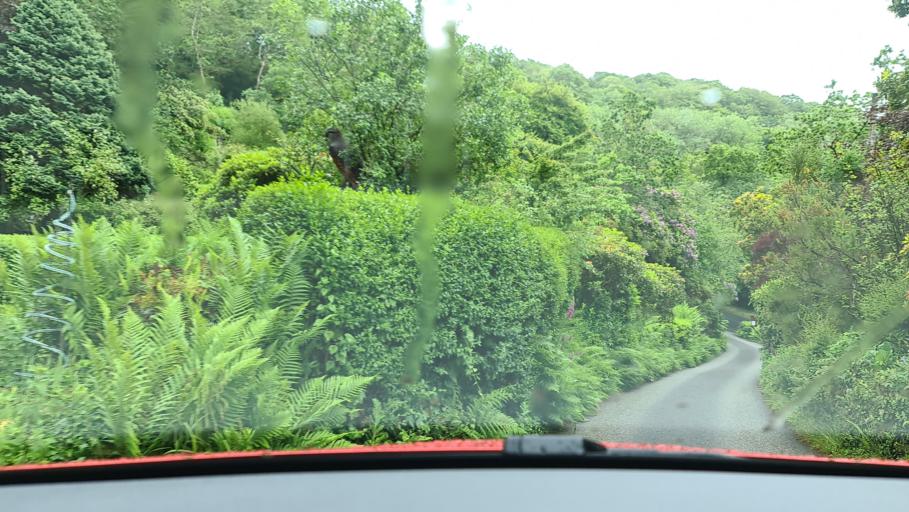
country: GB
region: England
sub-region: Cornwall
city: Liskeard
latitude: 50.4727
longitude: -4.5565
